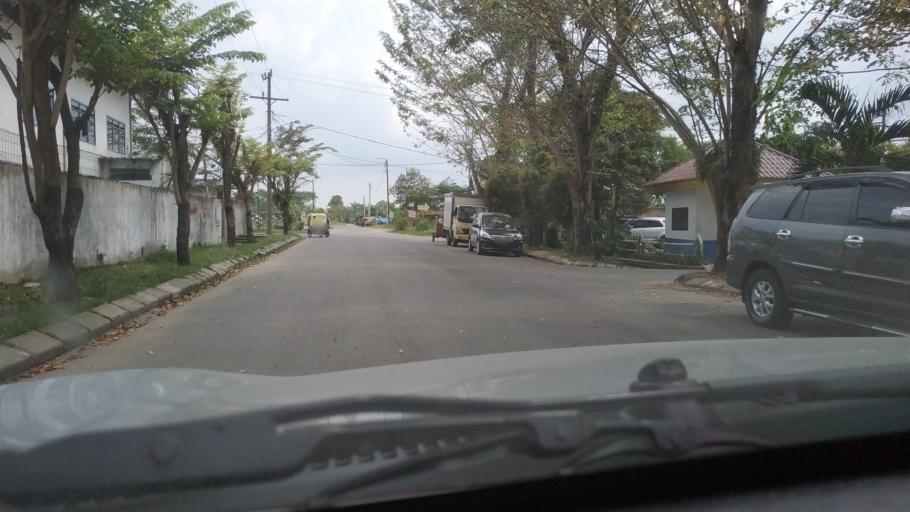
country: ID
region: North Sumatra
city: Sunggal
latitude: 3.5879
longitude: 98.6086
